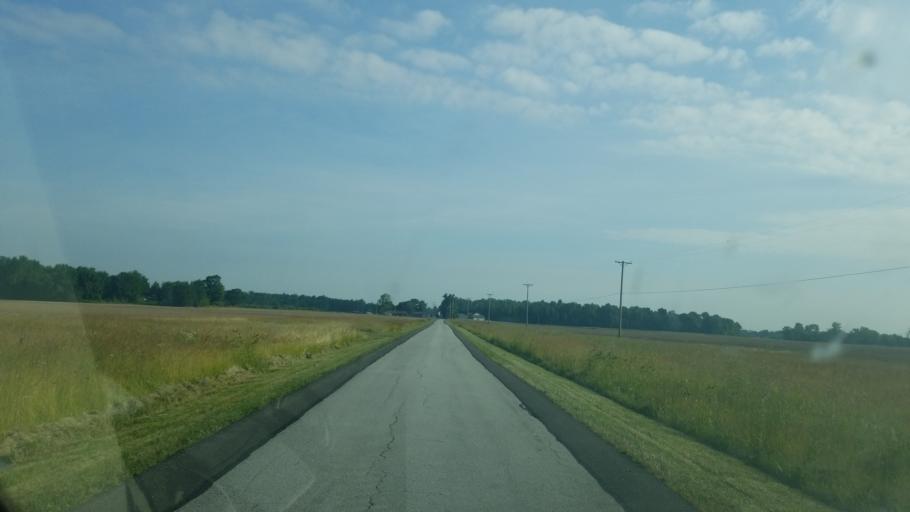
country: US
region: Ohio
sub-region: Hancock County
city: Arlington
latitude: 40.8281
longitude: -83.6707
